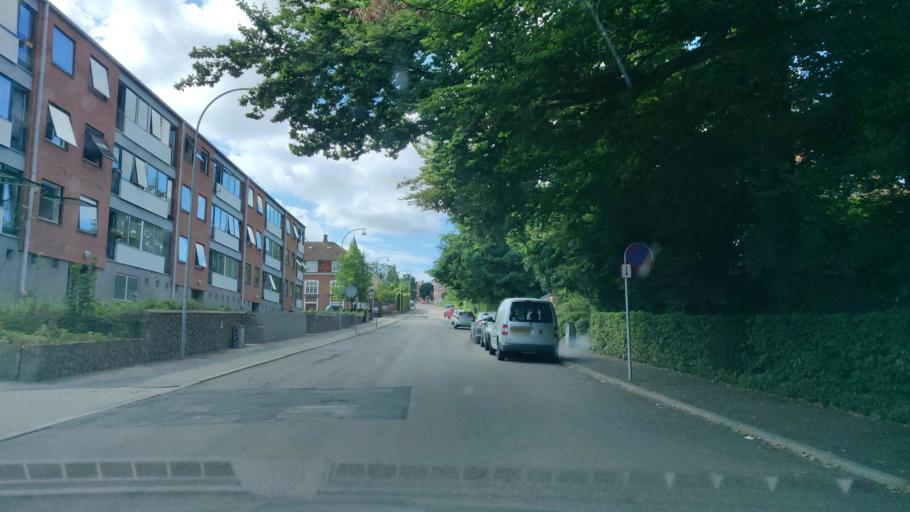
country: DK
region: Zealand
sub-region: Roskilde Kommune
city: Roskilde
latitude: 55.6470
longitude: 12.0835
